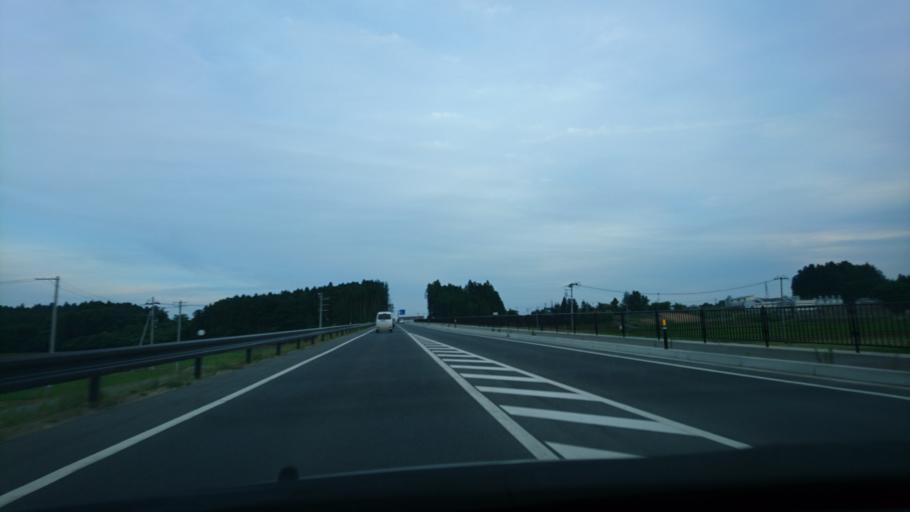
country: JP
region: Miyagi
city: Furukawa
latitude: 38.7465
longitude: 141.0363
